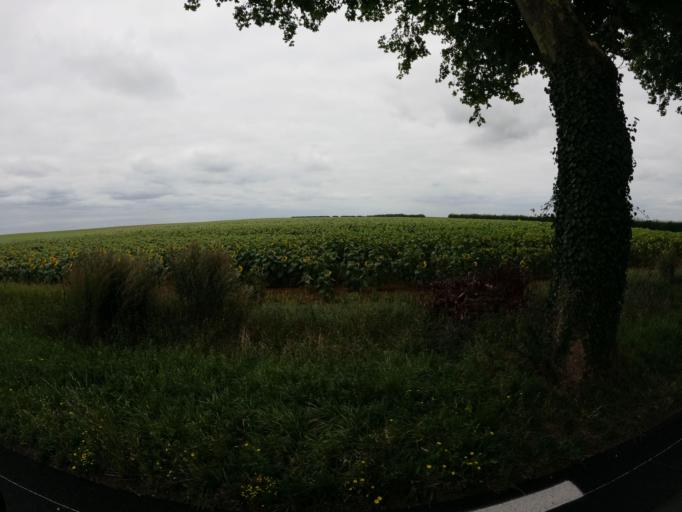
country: FR
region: Pays de la Loire
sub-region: Departement de la Vendee
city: Saint-Martin-sous-Mouzeuil
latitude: 46.5123
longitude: -0.9619
